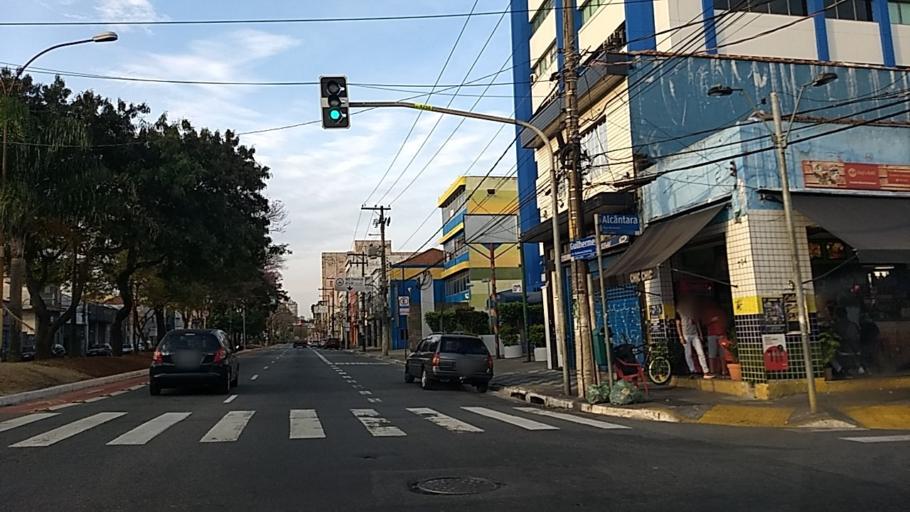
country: BR
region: Sao Paulo
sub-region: Sao Paulo
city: Sao Paulo
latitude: -23.5225
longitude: -46.5928
